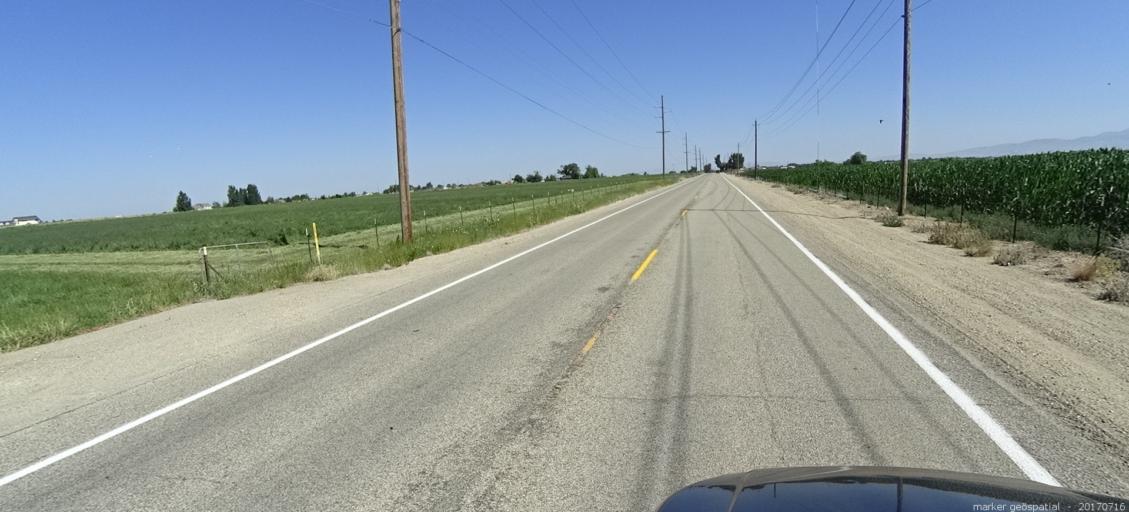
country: US
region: Idaho
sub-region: Ada County
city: Kuna
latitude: 43.5121
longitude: -116.3345
